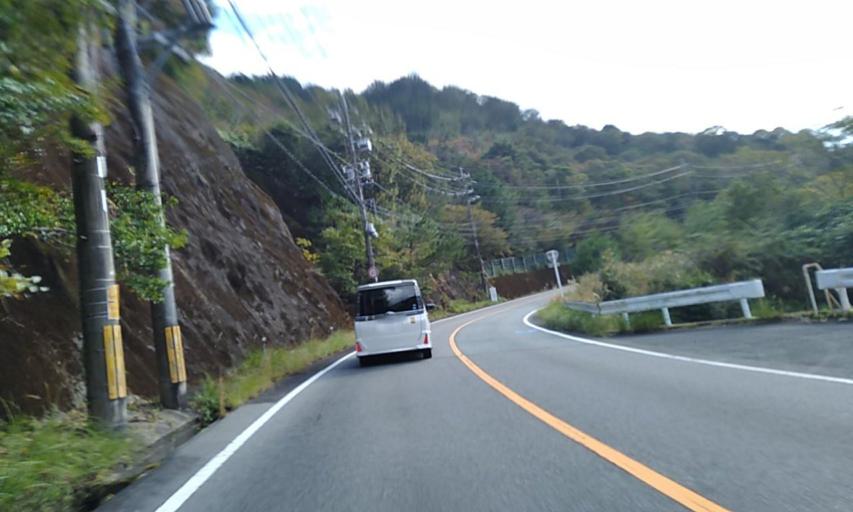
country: JP
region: Mie
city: Owase
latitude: 34.2127
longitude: 136.3551
